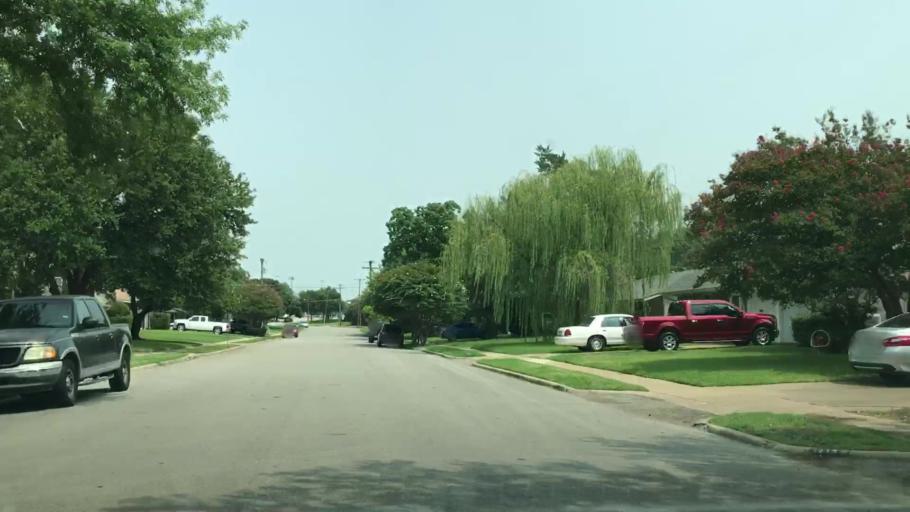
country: US
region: Texas
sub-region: Dallas County
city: Irving
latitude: 32.8512
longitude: -96.9643
